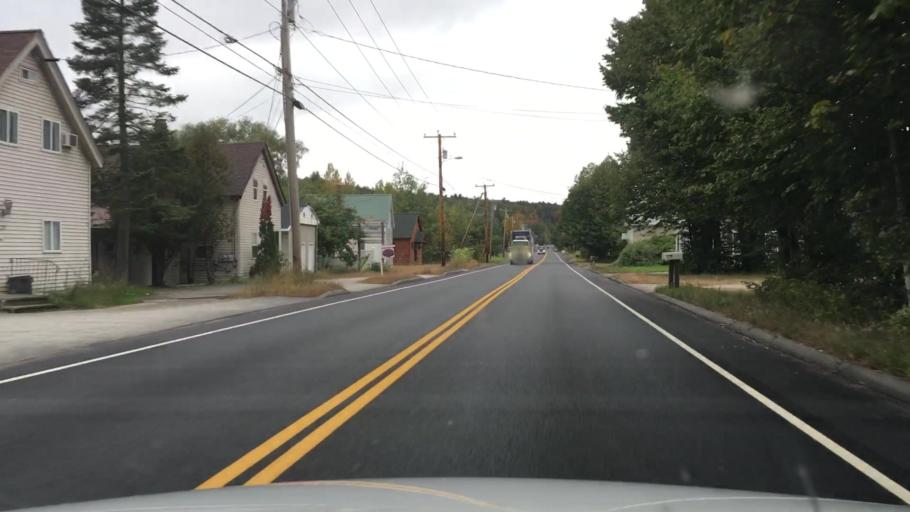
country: US
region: Maine
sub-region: Oxford County
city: Bethel
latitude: 44.4103
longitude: -70.8118
